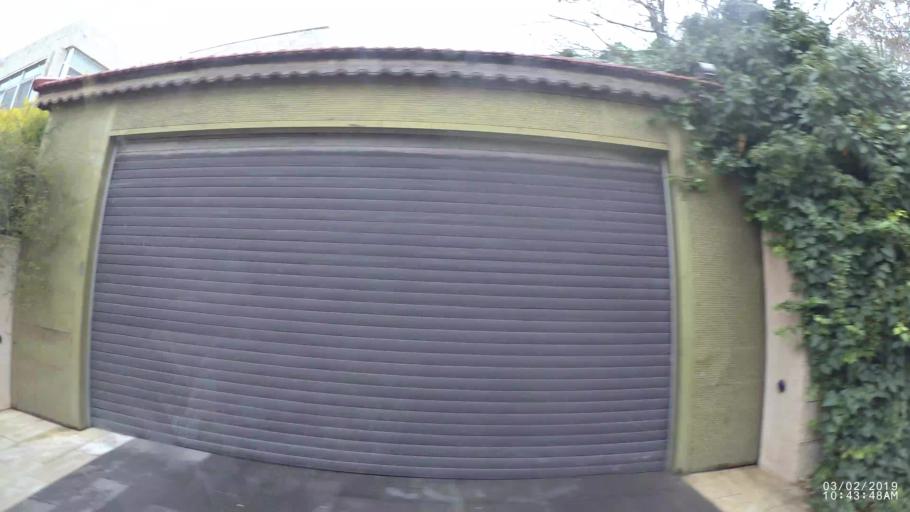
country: JO
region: Amman
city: Amman
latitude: 31.9508
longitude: 35.9296
